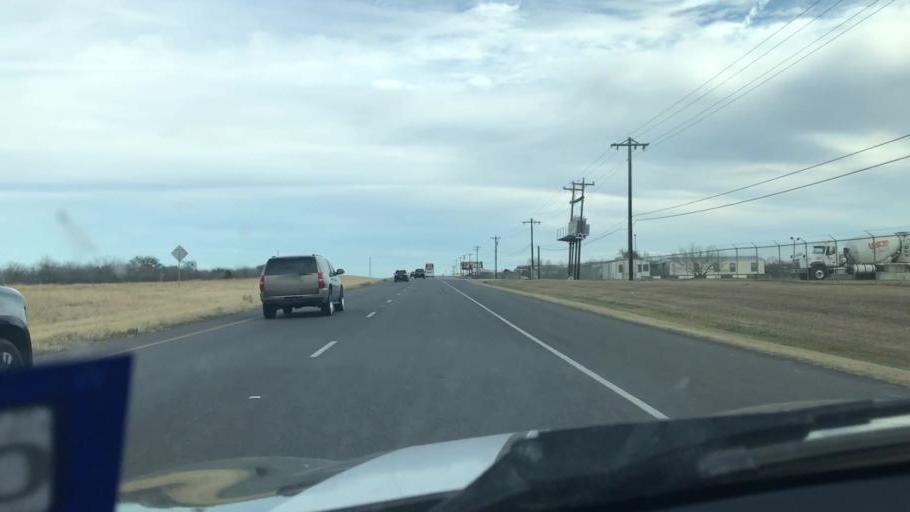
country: US
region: Texas
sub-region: Travis County
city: Manor
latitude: 30.3506
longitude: -97.4963
